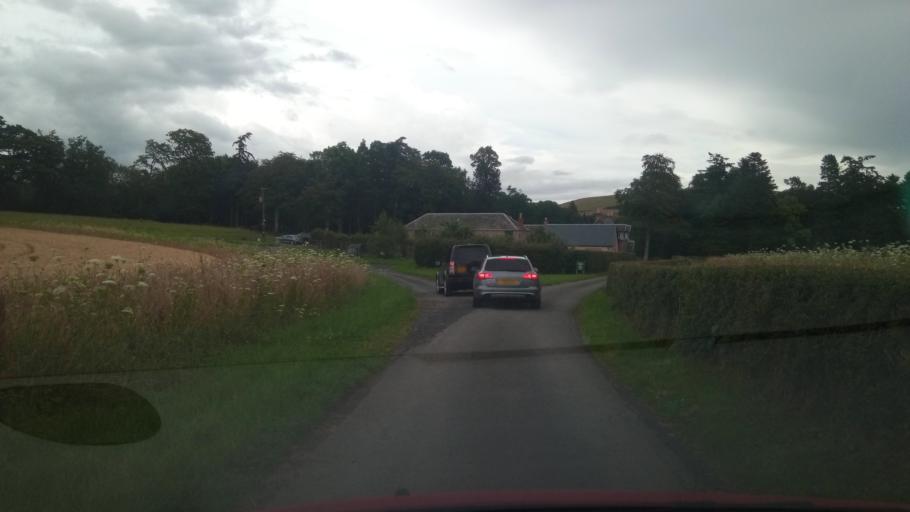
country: GB
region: Scotland
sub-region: The Scottish Borders
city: Newtown St Boswells
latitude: 55.5948
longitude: -2.6635
